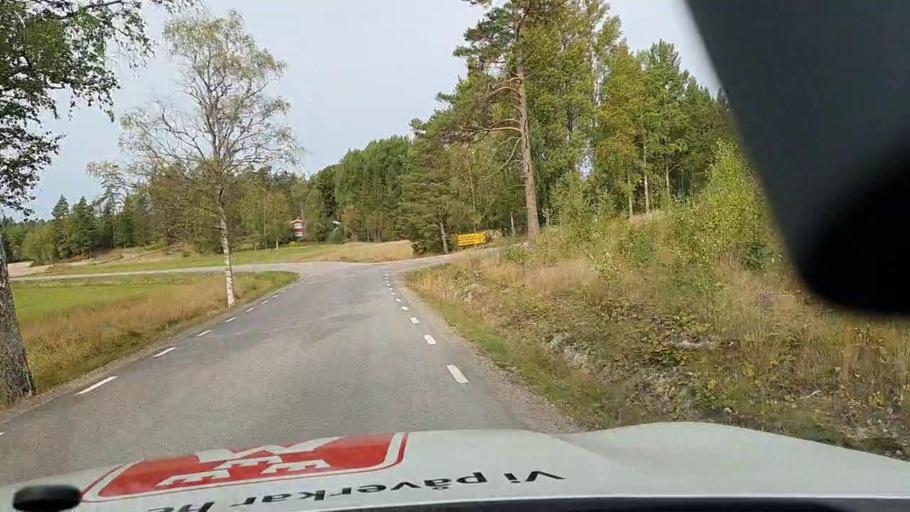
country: SE
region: Soedermanland
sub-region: Nykopings Kommun
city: Nykoping
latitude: 58.8552
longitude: 16.9618
